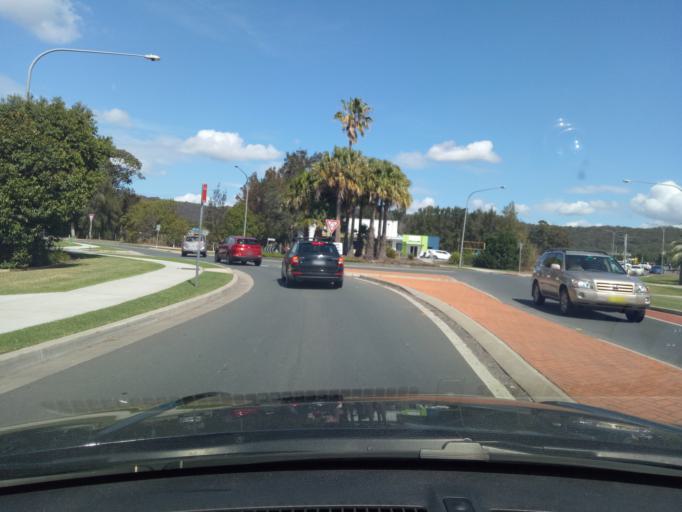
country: AU
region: New South Wales
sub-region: Wyong Shire
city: Tumbi Vmbi
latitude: -33.3631
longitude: 151.4433
